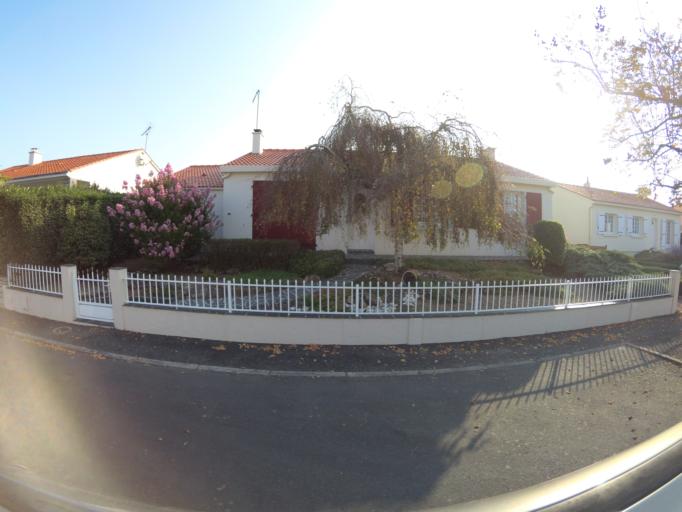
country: FR
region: Pays de la Loire
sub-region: Departement de la Vendee
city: Saint-Hilaire-de-Loulay
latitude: 47.0072
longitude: -1.3334
